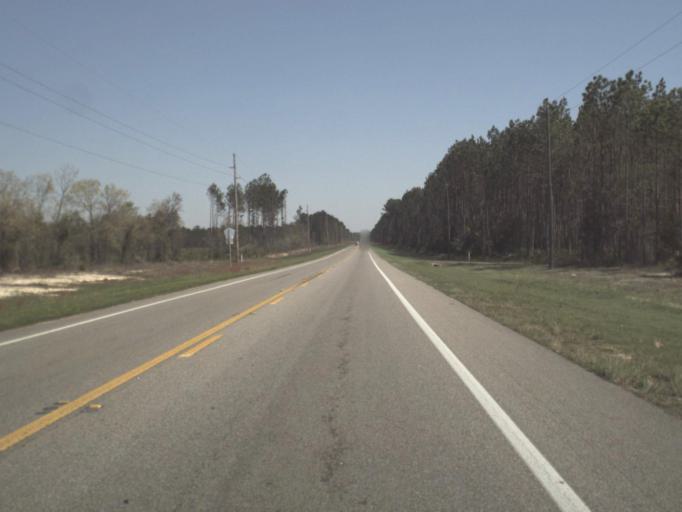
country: US
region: Florida
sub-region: Liberty County
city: Bristol
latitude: 30.4097
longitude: -84.8438
